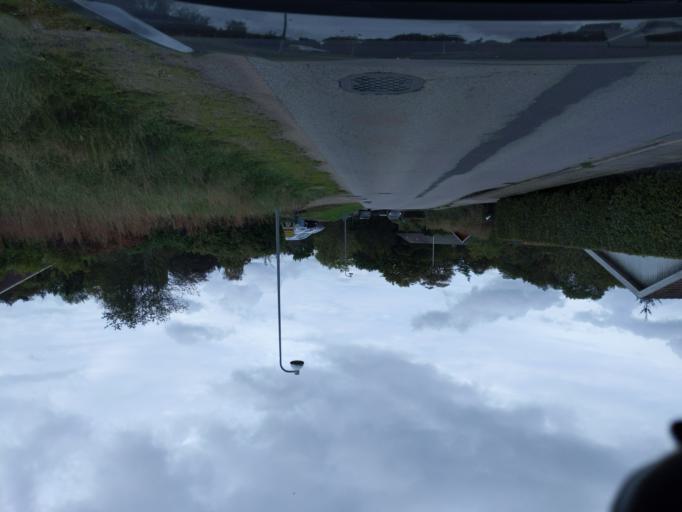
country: DK
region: Central Jutland
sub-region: Viborg Kommune
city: Viborg
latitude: 56.4222
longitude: 9.4445
